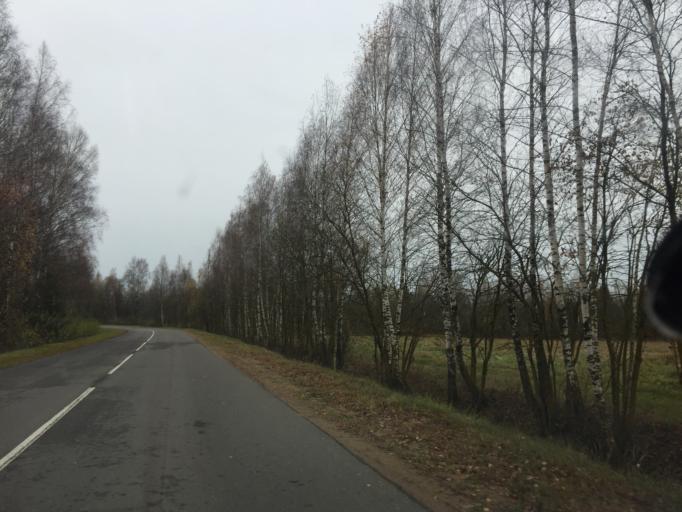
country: BY
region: Mogilev
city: Chavusy
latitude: 53.9434
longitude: 31.0436
